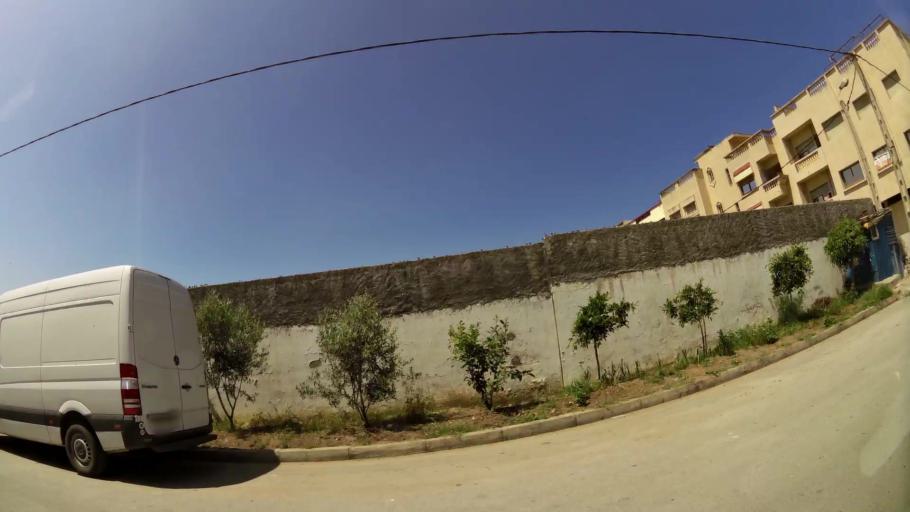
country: MA
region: Rabat-Sale-Zemmour-Zaer
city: Sale
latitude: 34.0768
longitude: -6.7849
